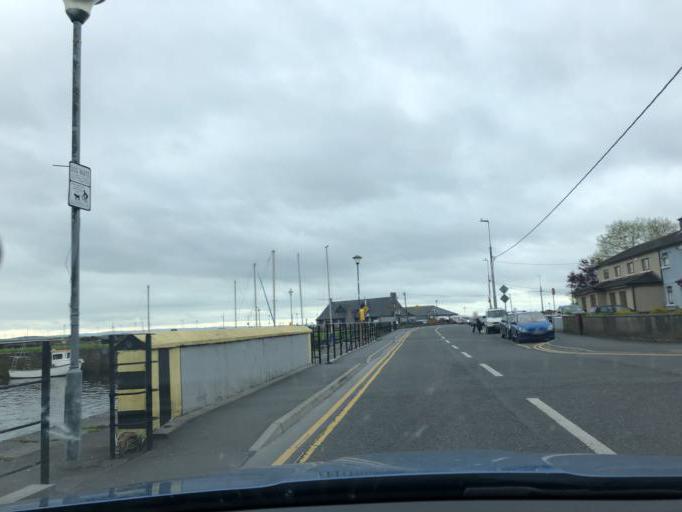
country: IE
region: Connaught
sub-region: County Galway
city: Gaillimh
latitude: 53.2684
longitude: -9.0552
